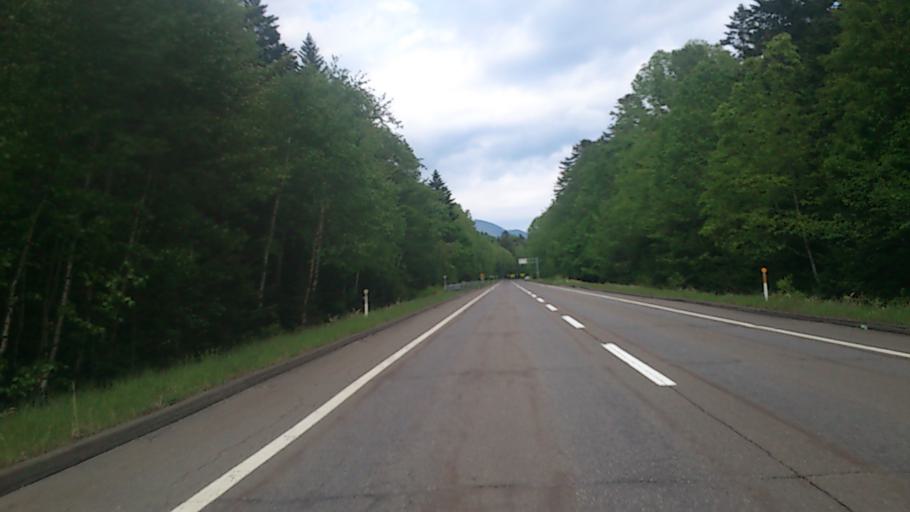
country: JP
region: Hokkaido
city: Kitami
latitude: 43.4056
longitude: 143.9425
